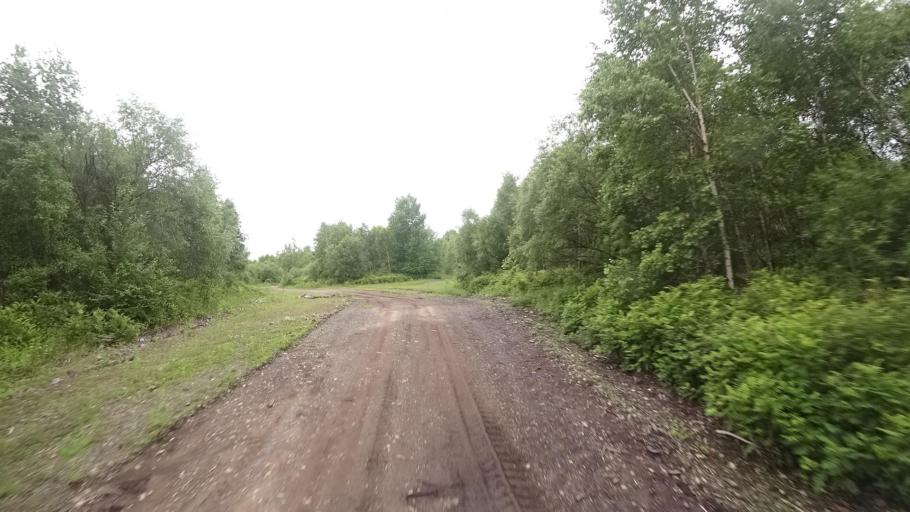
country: RU
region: Khabarovsk Krai
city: Amursk
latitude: 49.9126
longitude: 136.1583
